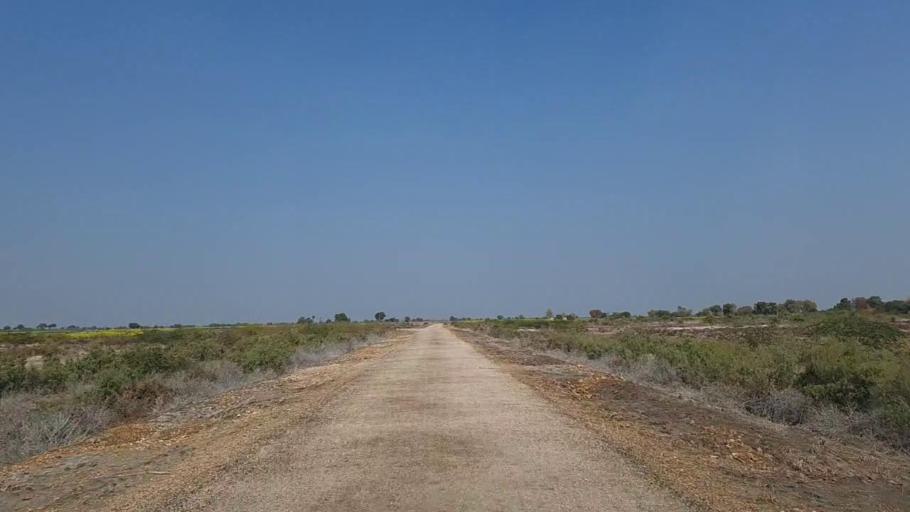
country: PK
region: Sindh
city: Nawabshah
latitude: 26.2913
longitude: 68.4810
